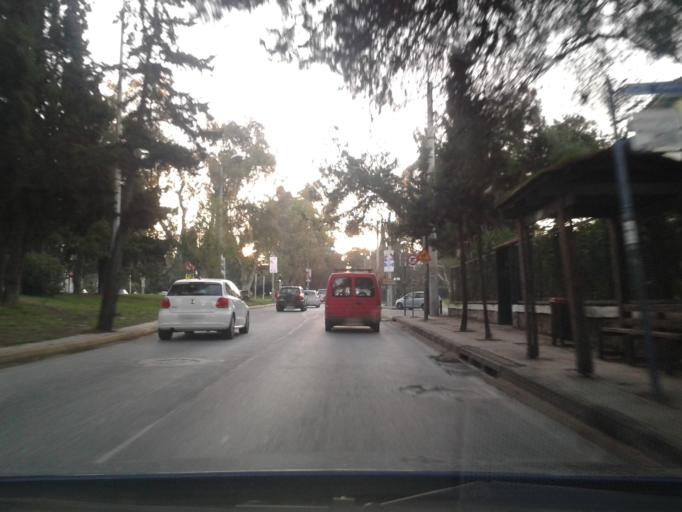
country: GR
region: Attica
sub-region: Nomarchia Athinas
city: Filothei
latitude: 38.0286
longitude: 23.7814
